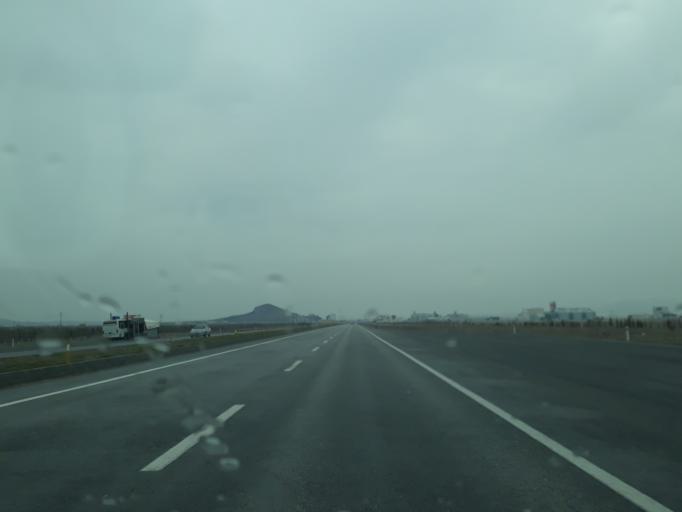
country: TR
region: Konya
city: Karapinar
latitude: 37.7120
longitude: 33.6104
